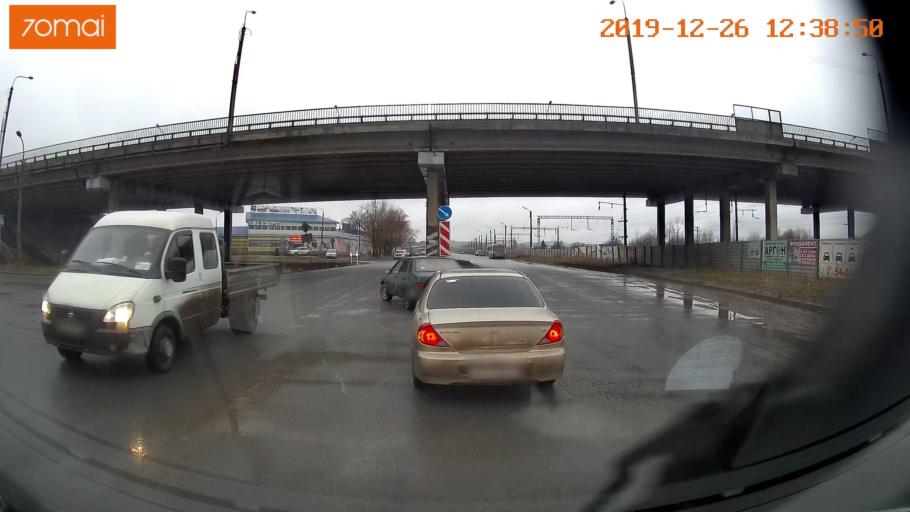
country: RU
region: Vologda
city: Tonshalovo
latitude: 59.1359
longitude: 37.9787
